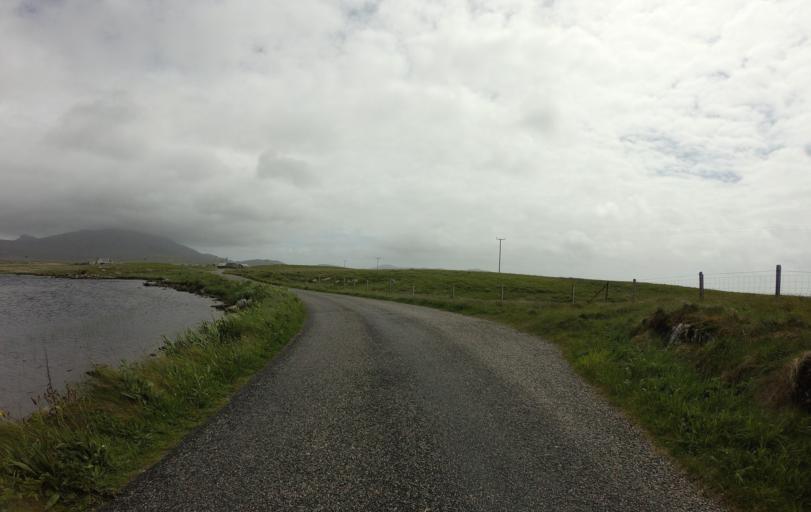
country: GB
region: Scotland
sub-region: Eilean Siar
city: Isle of South Uist
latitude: 57.2725
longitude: -7.4017
